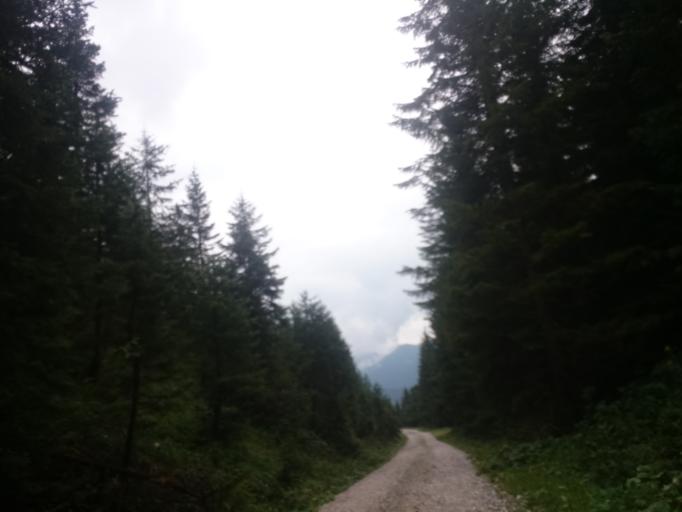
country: AT
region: Tyrol
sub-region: Politischer Bezirk Innsbruck Land
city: Thaur
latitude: 47.4192
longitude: 11.4832
